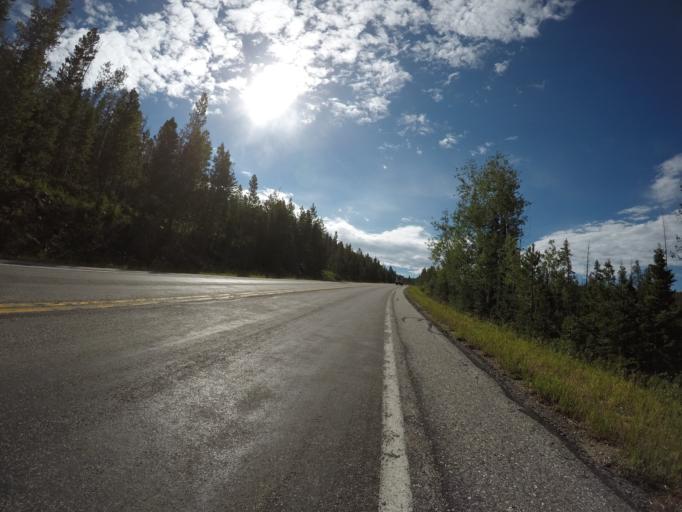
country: US
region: Wyoming
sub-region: Carbon County
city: Saratoga
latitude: 41.3292
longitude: -106.4762
